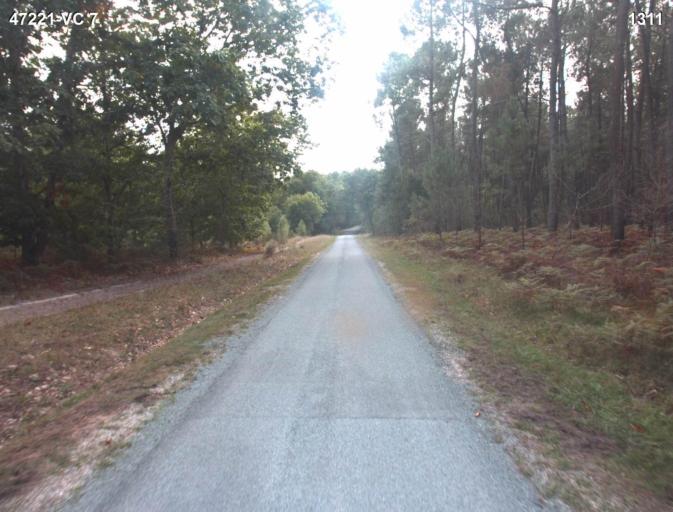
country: FR
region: Aquitaine
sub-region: Departement du Lot-et-Garonne
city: Mezin
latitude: 44.0884
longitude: 0.2247
